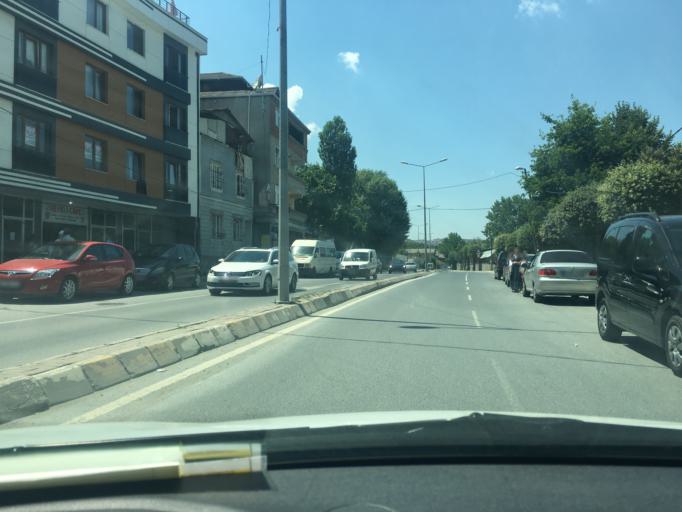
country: TR
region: Istanbul
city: Sisli
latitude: 41.0869
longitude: 28.9370
